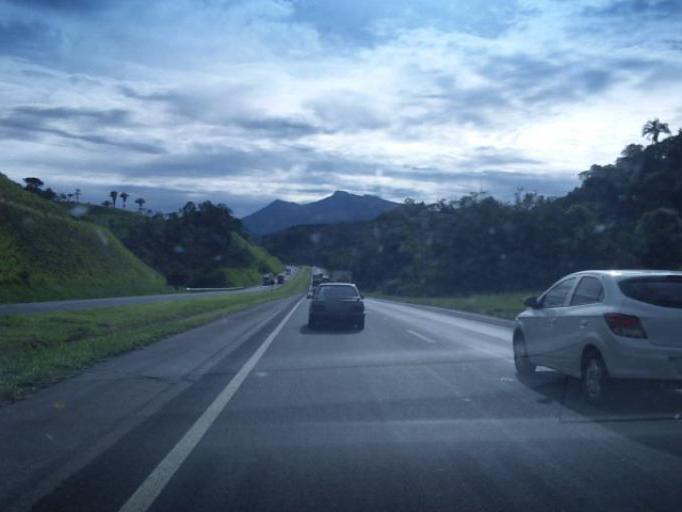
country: BR
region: Parana
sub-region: Antonina
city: Antonina
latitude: -25.1010
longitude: -48.7322
